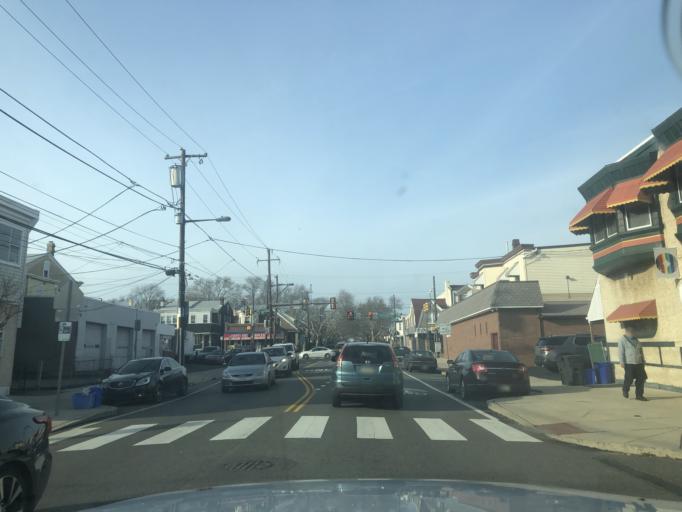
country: US
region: New Jersey
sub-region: Burlington County
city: Palmyra
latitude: 40.0277
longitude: -75.0384
